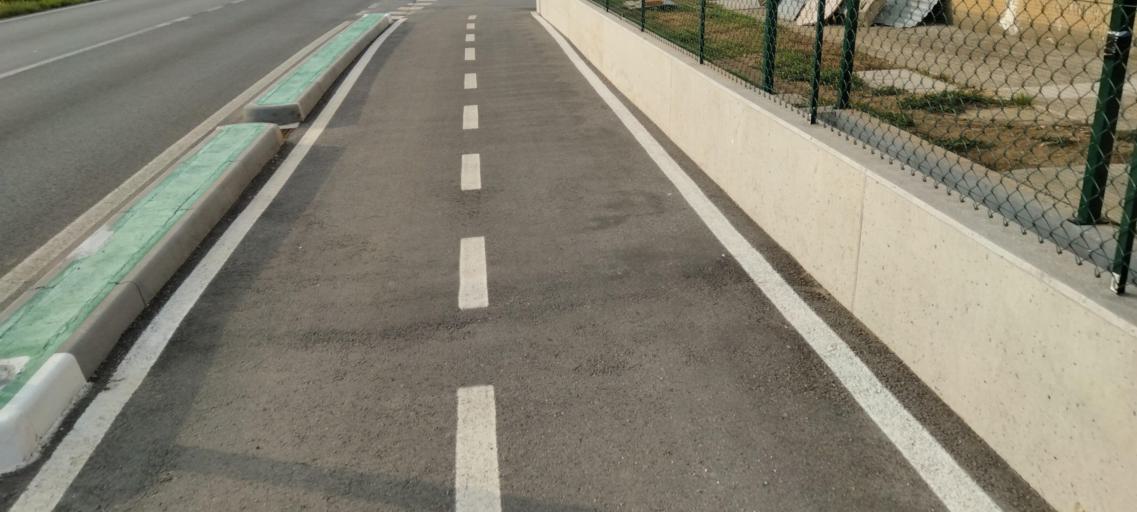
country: IT
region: Veneto
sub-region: Provincia di Vicenza
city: Costabissara
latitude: 45.5959
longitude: 11.4766
